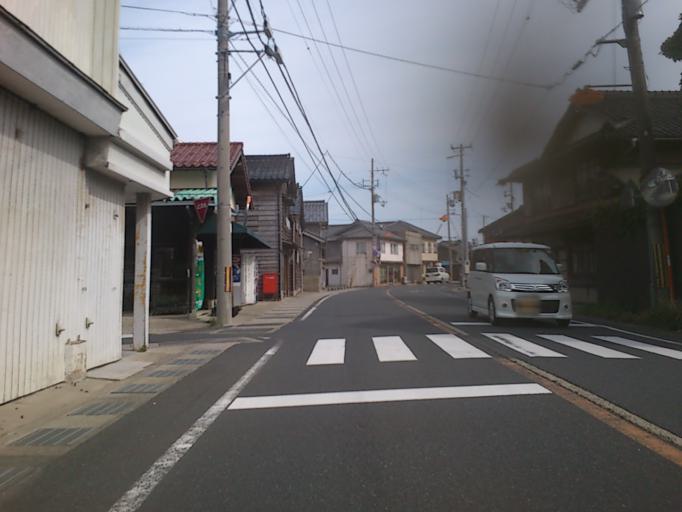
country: JP
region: Kyoto
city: Miyazu
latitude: 35.6856
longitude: 135.0239
